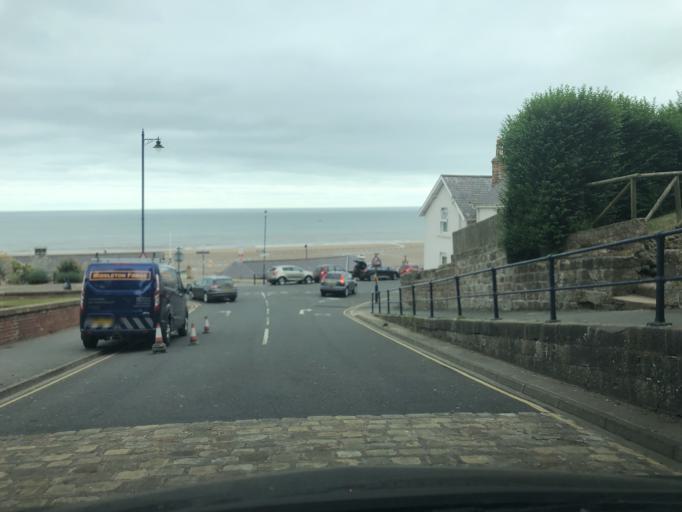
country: GB
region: England
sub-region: North Yorkshire
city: Filey
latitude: 54.2089
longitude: -0.2858
